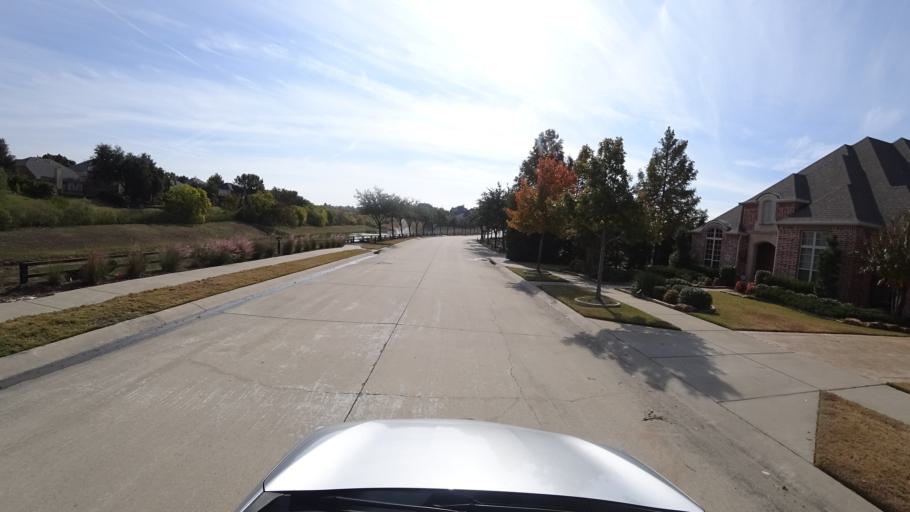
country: US
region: Texas
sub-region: Denton County
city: The Colony
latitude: 33.0398
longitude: -96.8878
